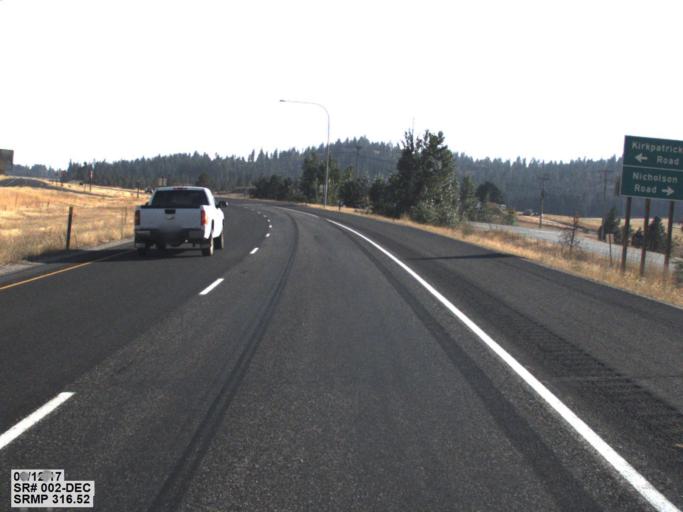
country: US
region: Washington
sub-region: Spokane County
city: Deer Park
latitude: 48.0619
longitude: -117.3447
